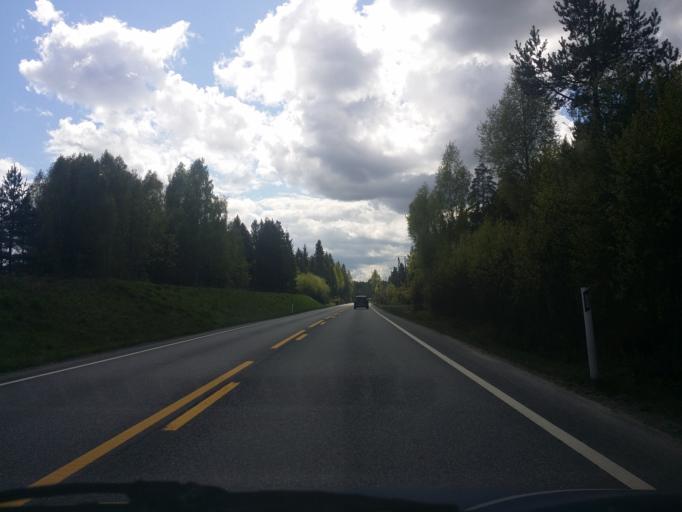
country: NO
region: Buskerud
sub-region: Modum
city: Vikersund
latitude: 59.9572
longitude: 9.9773
